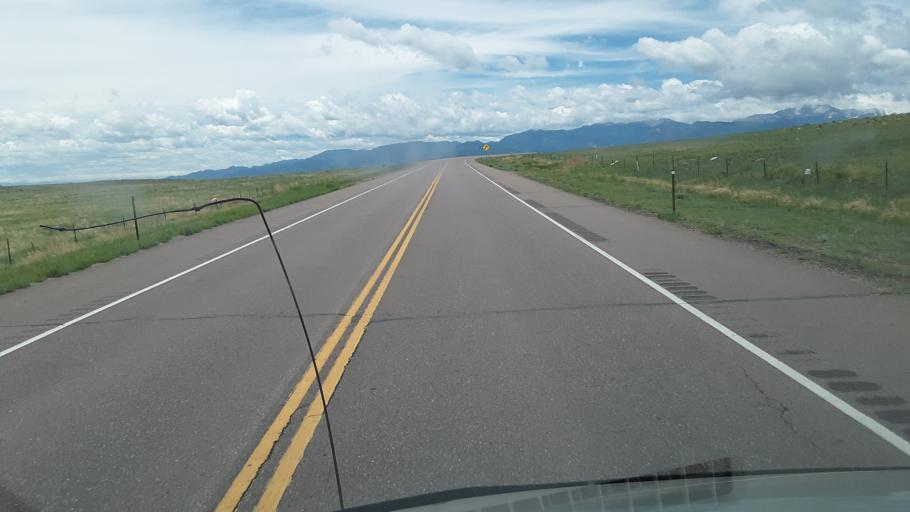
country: US
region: Colorado
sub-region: El Paso County
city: Cimarron Hills
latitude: 38.8362
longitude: -104.6387
